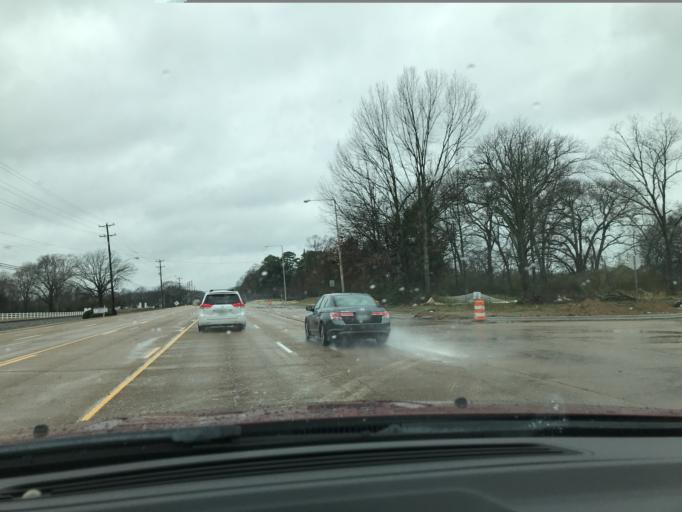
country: US
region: Tennessee
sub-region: Shelby County
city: Collierville
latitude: 35.0468
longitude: -89.7075
